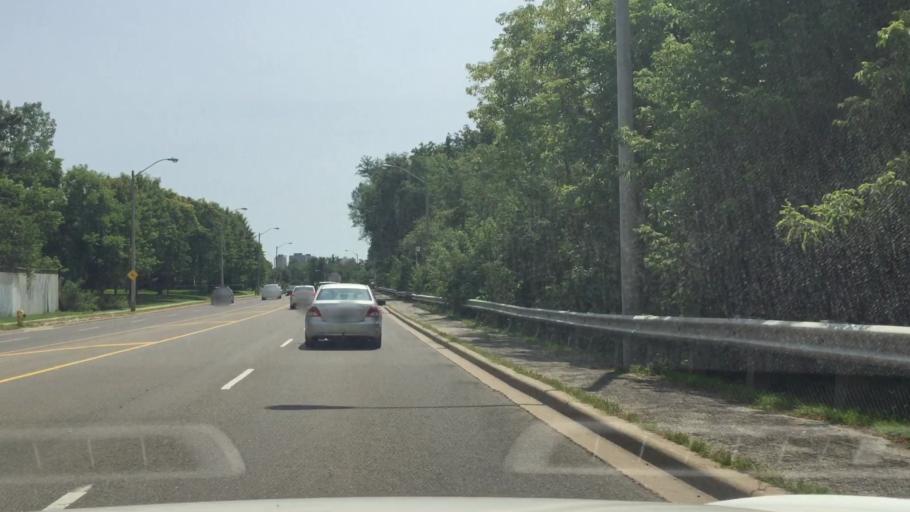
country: CA
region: Ontario
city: Willowdale
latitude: 43.7291
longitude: -79.3532
